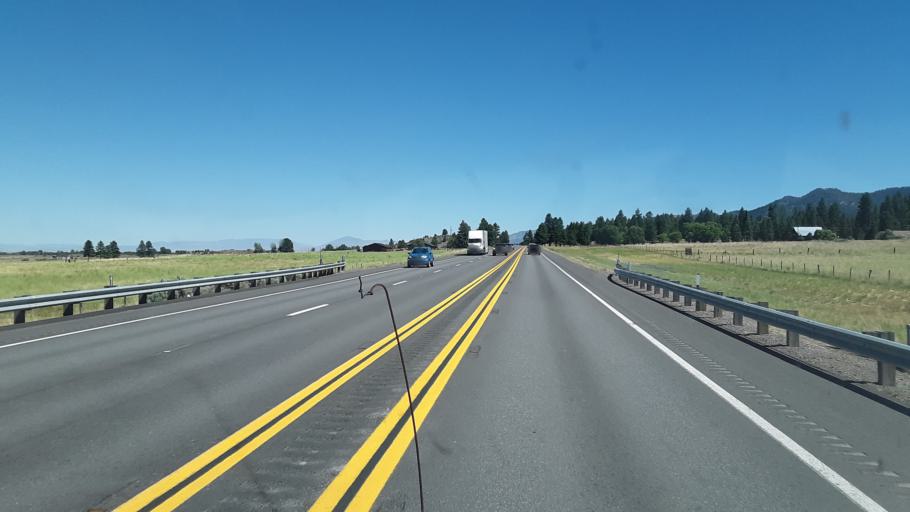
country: US
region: California
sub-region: Lassen County
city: Janesville
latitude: 40.3112
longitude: -120.5350
